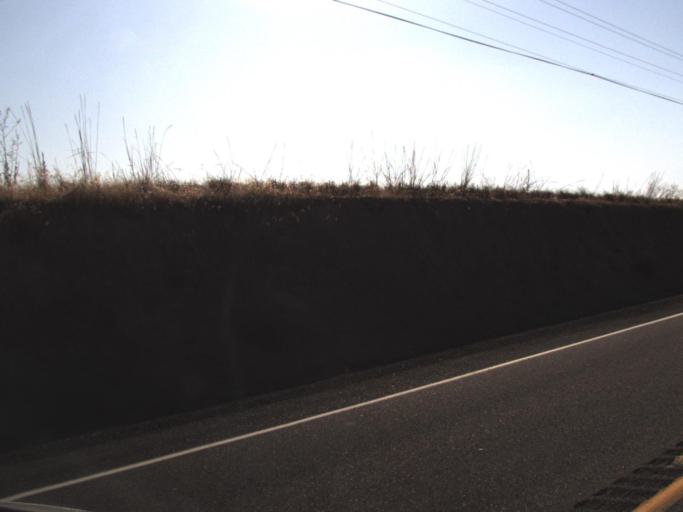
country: US
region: Washington
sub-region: Walla Walla County
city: Garrett
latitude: 46.2962
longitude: -118.5931
